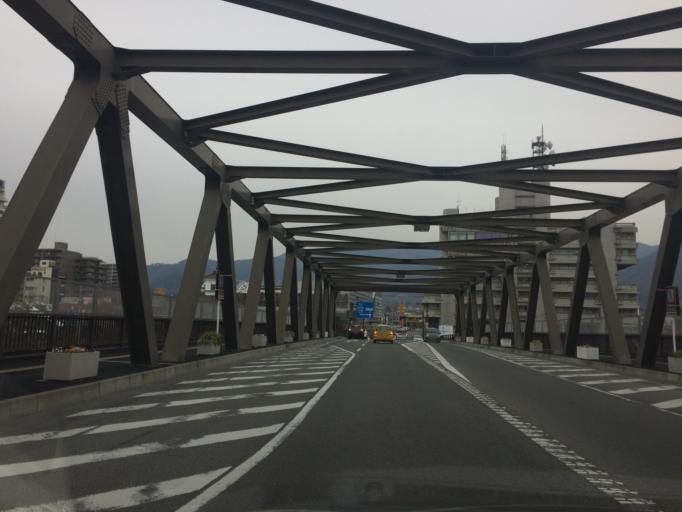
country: JP
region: Yamanashi
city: Kofu-shi
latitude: 35.6666
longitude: 138.5701
